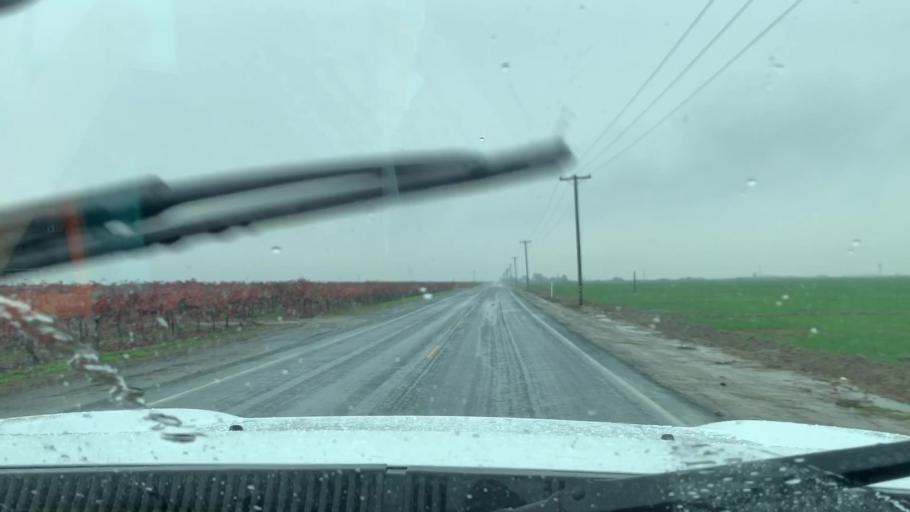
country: US
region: California
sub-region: Tulare County
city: Earlimart
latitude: 35.8919
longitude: -119.2967
